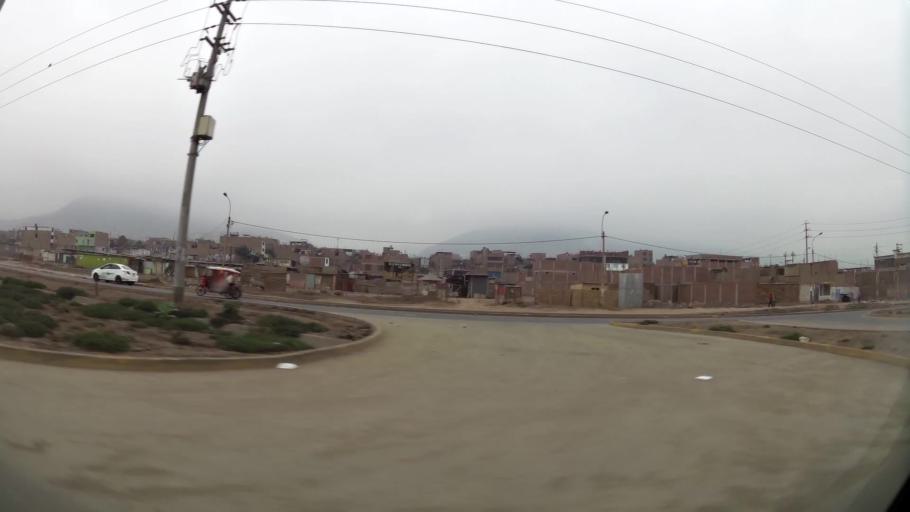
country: PE
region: Lima
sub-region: Lima
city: Urb. Santo Domingo
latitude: -11.8710
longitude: -77.0217
